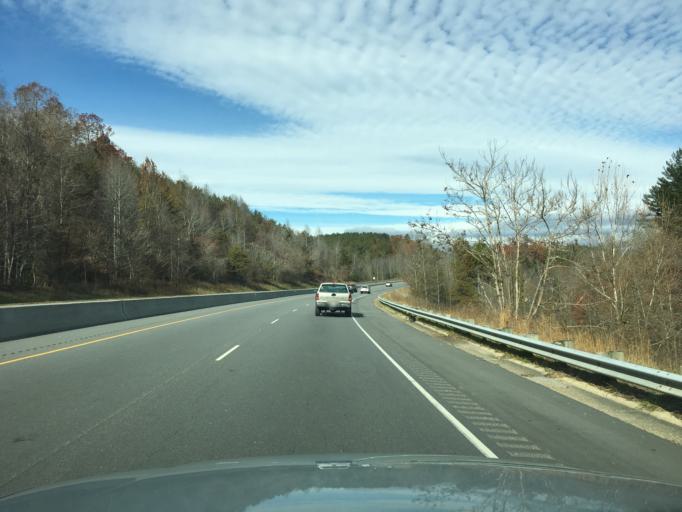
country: US
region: North Carolina
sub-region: McDowell County
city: Marion
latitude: 35.6859
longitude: -82.0301
